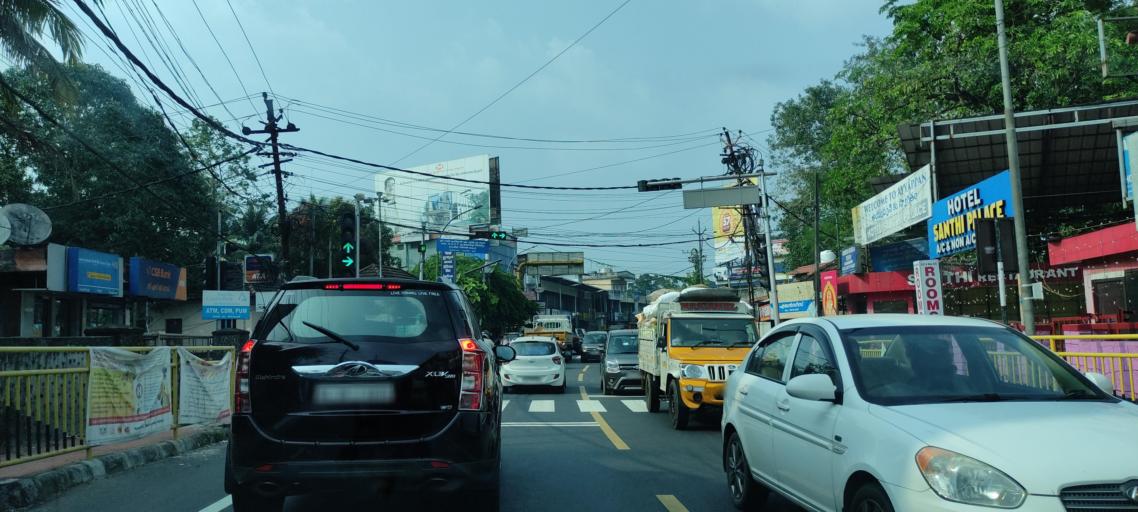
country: IN
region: Kerala
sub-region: Alappuzha
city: Chengannur
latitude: 9.3205
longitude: 76.6104
